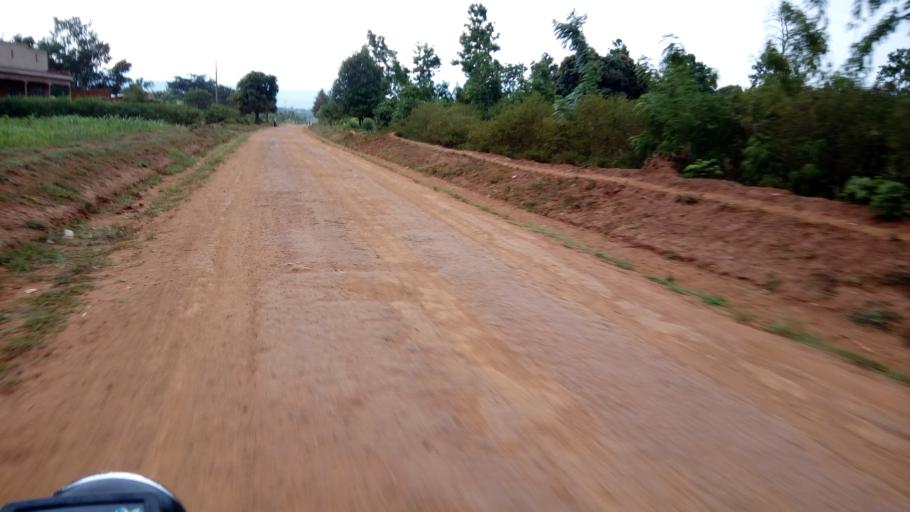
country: UG
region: Eastern Region
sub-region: Mbale District
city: Mbale
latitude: 1.1405
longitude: 34.1267
